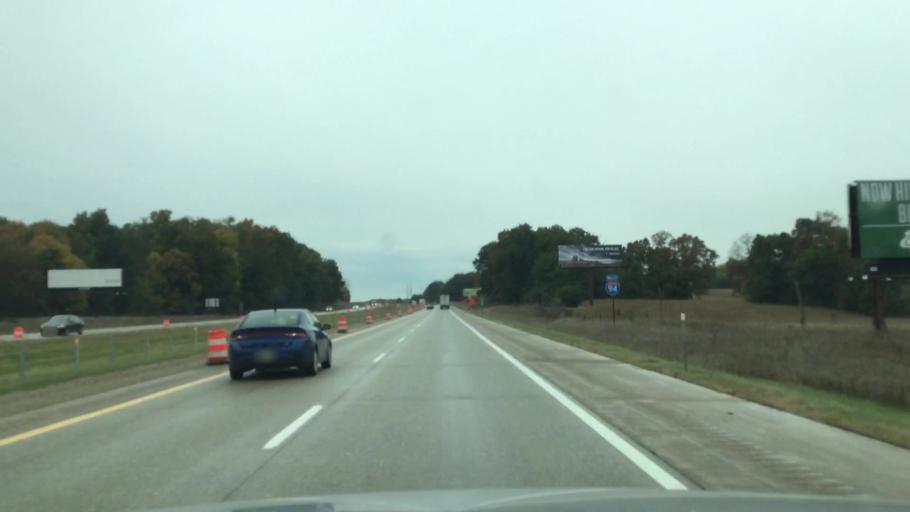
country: US
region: Michigan
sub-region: Calhoun County
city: Albion
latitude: 42.2641
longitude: -84.7192
